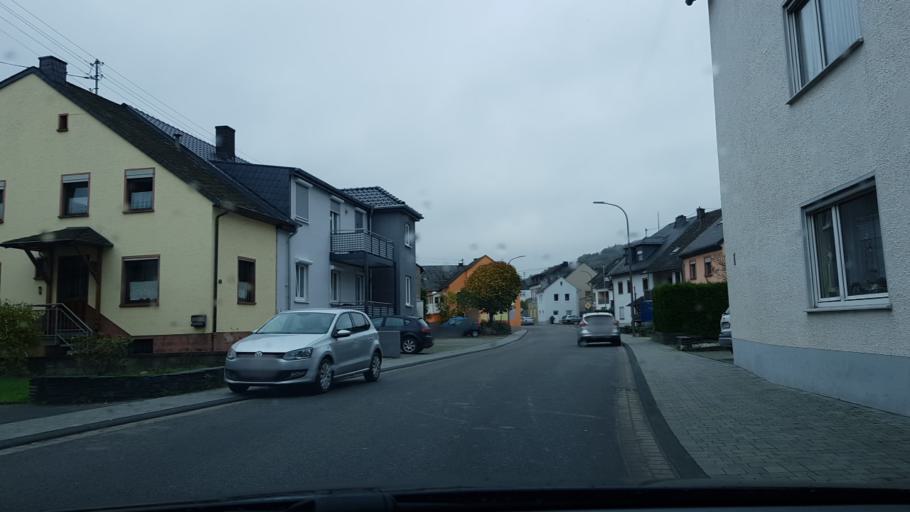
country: DE
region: Rheinland-Pfalz
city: Fell
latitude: 49.7721
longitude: 6.7818
